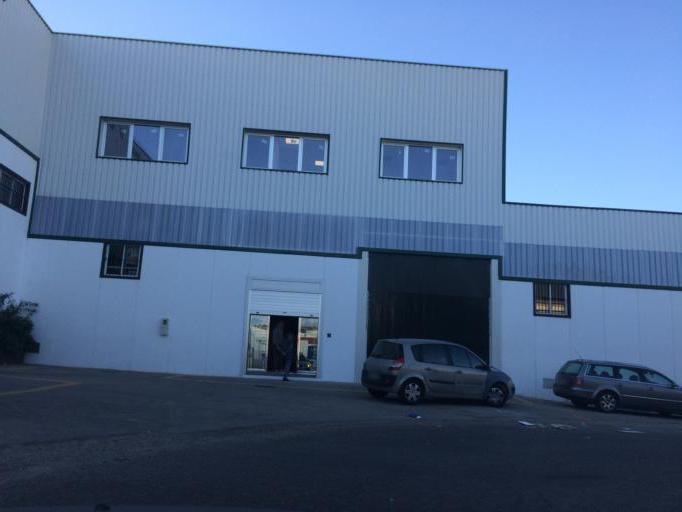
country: ES
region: Andalusia
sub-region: Provincia de Almeria
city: Viator
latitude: 36.8808
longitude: -2.4172
